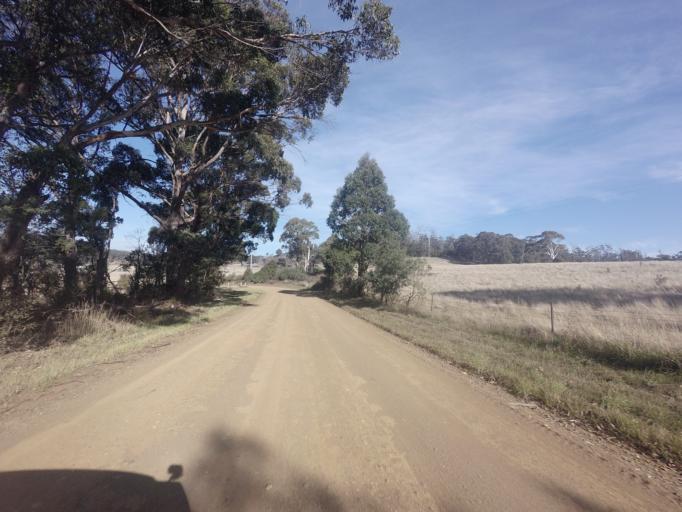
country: AU
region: Tasmania
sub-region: Sorell
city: Sorell
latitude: -42.4778
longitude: 147.4755
